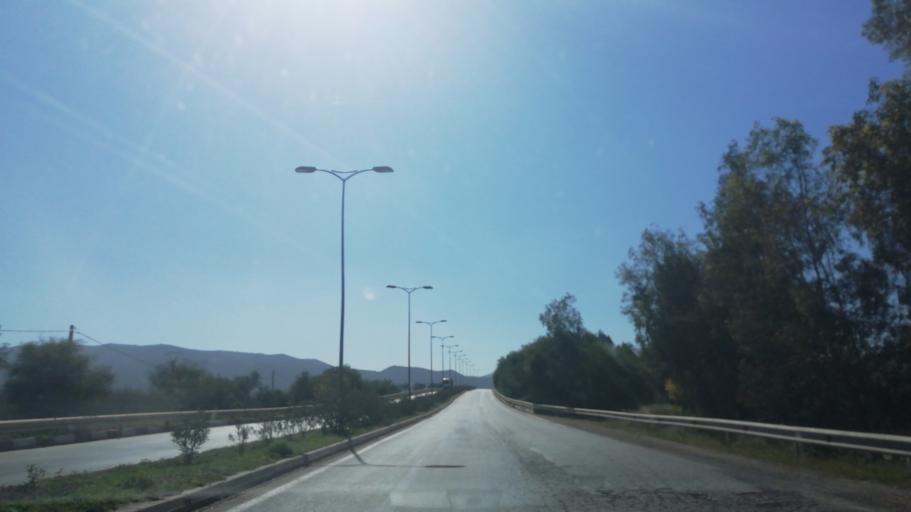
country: DZ
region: Mascara
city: Sig
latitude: 35.5419
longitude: -0.2044
